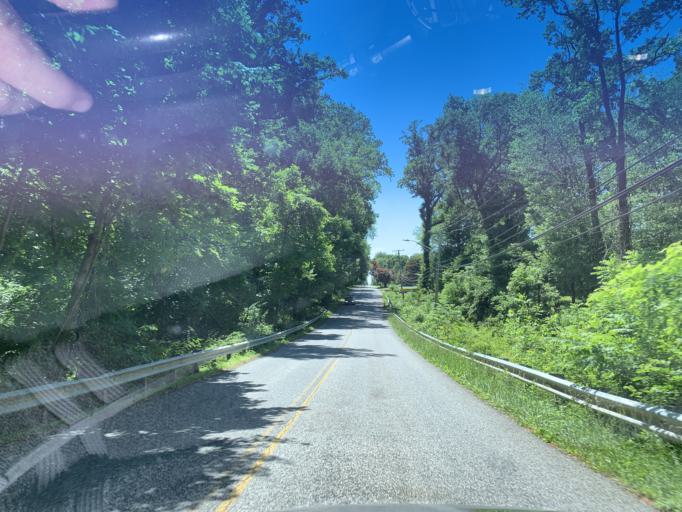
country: US
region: Maryland
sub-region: Harford County
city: Havre de Grace
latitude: 39.5555
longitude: -76.1328
